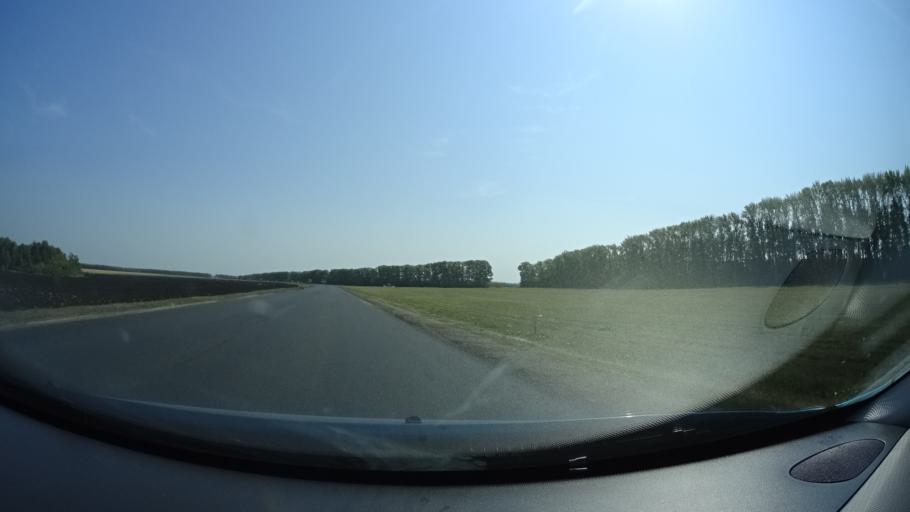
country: RU
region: Bashkortostan
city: Karmaskaly
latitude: 54.3871
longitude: 56.1375
